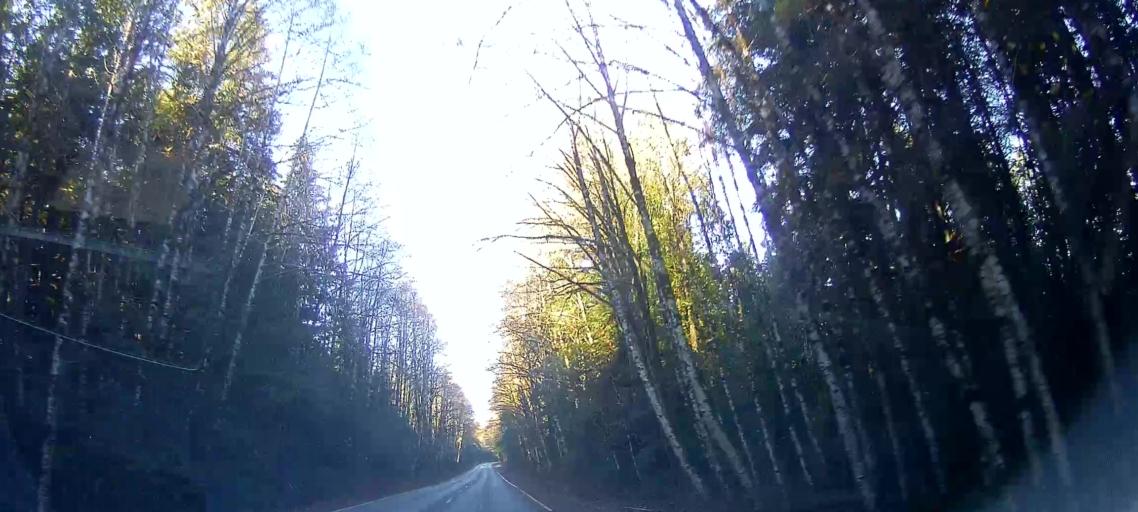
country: US
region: Washington
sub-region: Snohomish County
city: Darrington
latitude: 48.6112
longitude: -121.7547
